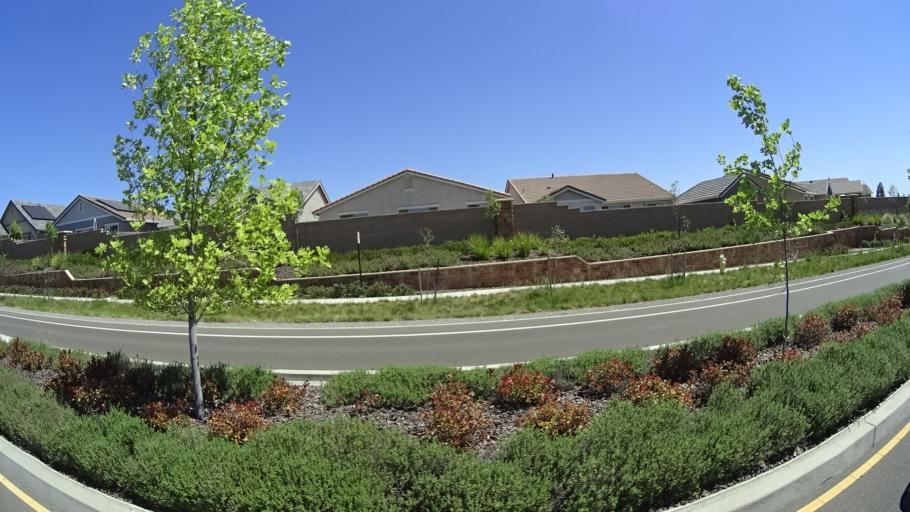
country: US
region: California
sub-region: Placer County
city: Rocklin
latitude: 38.8270
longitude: -121.2671
